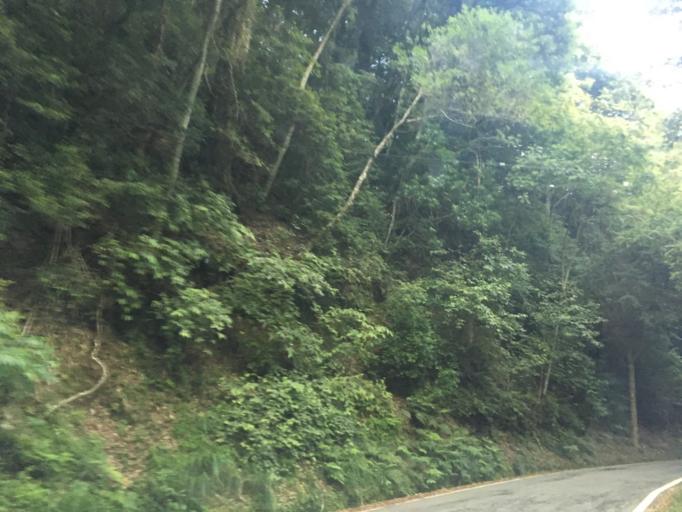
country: TW
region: Taiwan
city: Fengyuan
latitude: 24.2384
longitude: 120.9777
